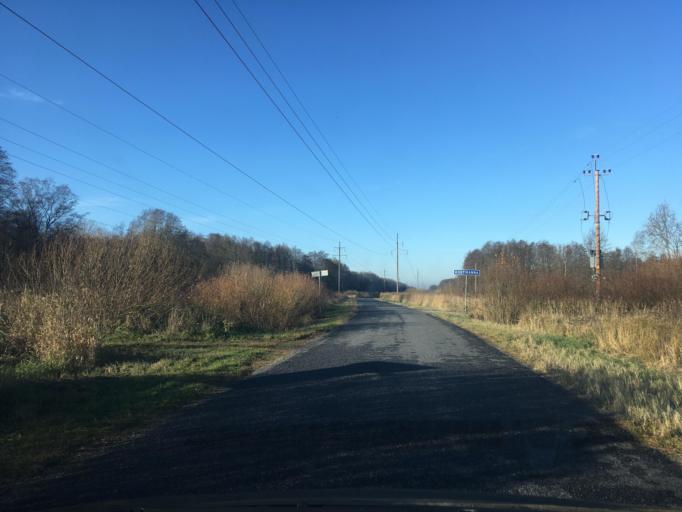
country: EE
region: Harju
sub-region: Maardu linn
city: Maardu
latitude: 59.4780
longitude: 25.1126
